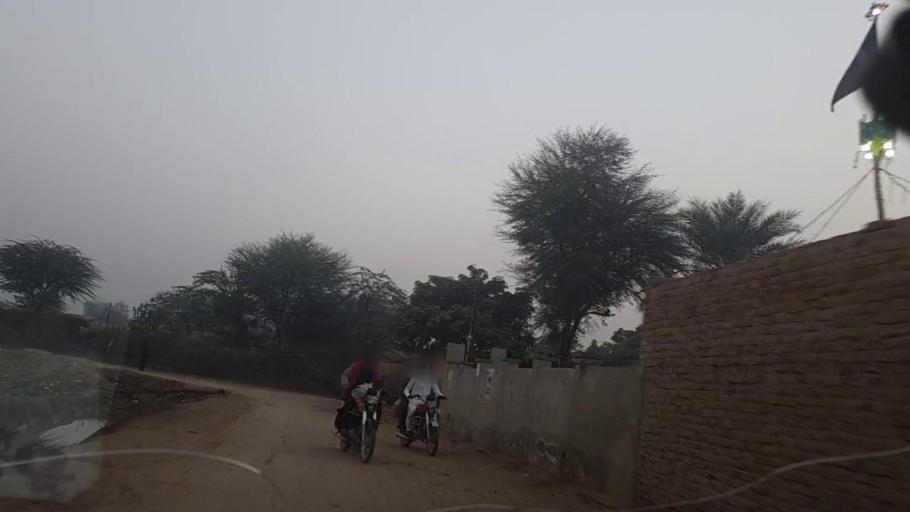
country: PK
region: Sindh
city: Hingorja
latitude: 27.2208
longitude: 68.4279
